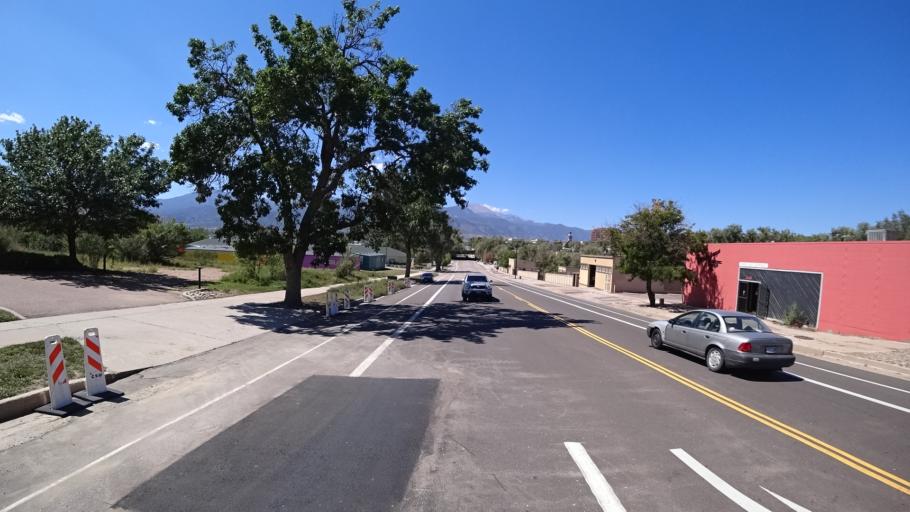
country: US
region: Colorado
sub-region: El Paso County
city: Colorado Springs
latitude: 38.8279
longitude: -104.8136
